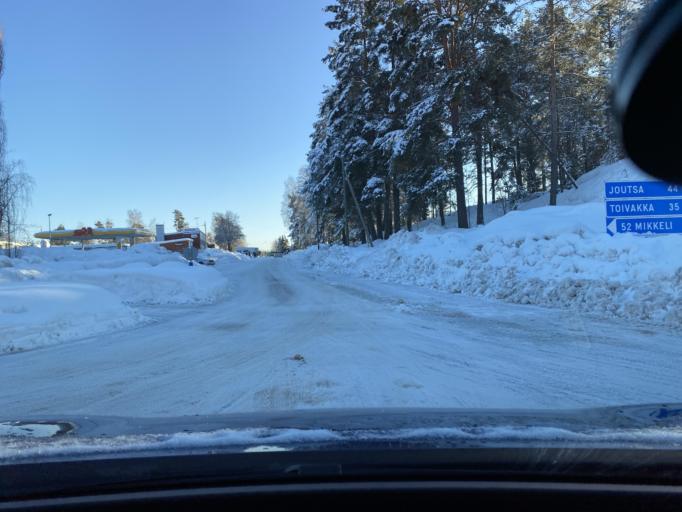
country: FI
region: Southern Savonia
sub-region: Mikkeli
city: Kangasniemi
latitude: 61.9909
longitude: 26.6343
